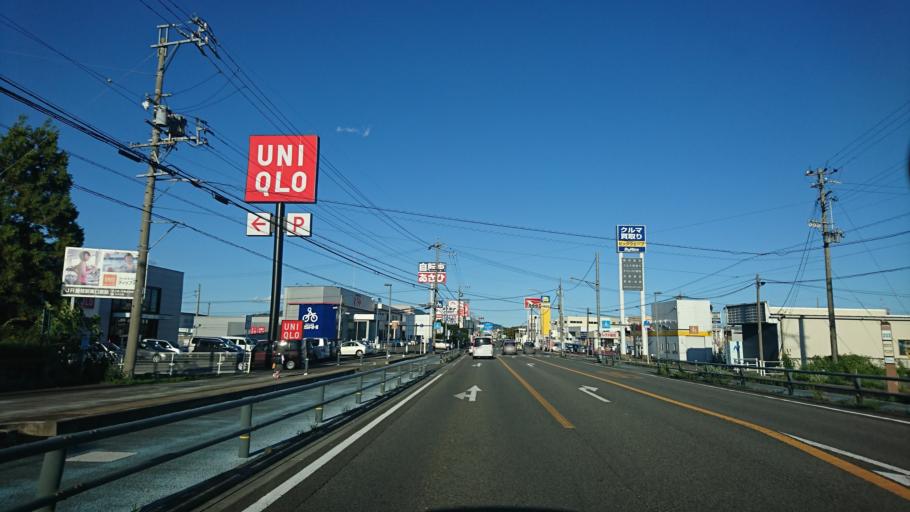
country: JP
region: Shizuoka
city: Fujieda
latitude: 34.8506
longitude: 138.2390
